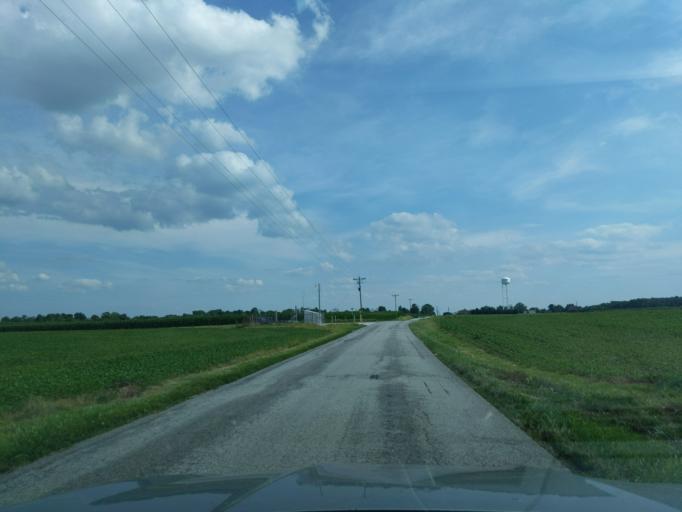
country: US
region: Indiana
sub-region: Decatur County
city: Greensburg
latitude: 39.2791
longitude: -85.4652
